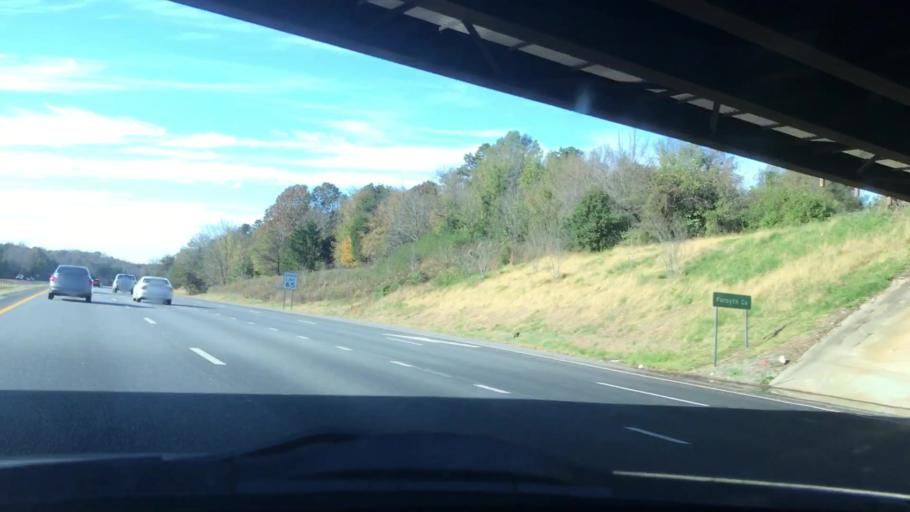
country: US
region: North Carolina
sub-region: Guilford County
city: High Point
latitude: 36.0172
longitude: -80.0434
